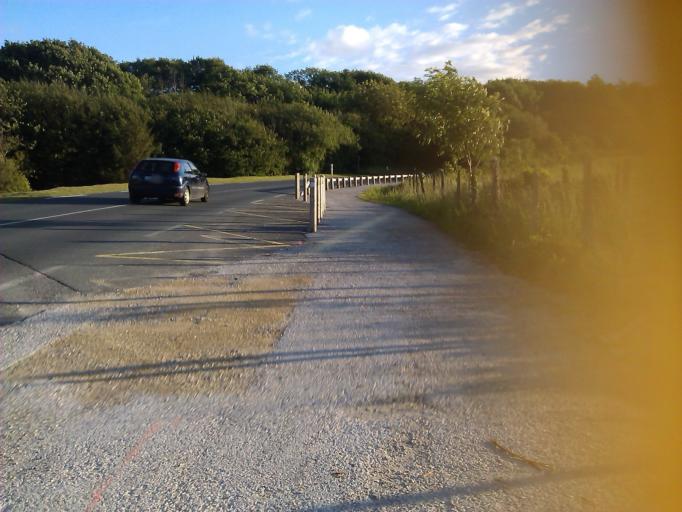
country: FR
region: Aquitaine
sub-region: Departement des Pyrenees-Atlantiques
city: Hendaye
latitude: 43.3770
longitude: -1.7392
